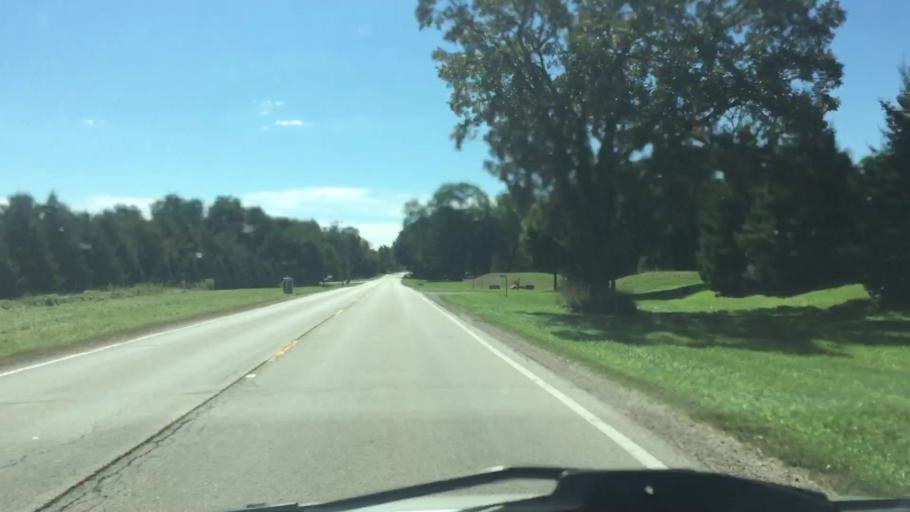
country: US
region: Wisconsin
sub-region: Waukesha County
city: North Prairie
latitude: 42.9613
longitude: -88.4049
